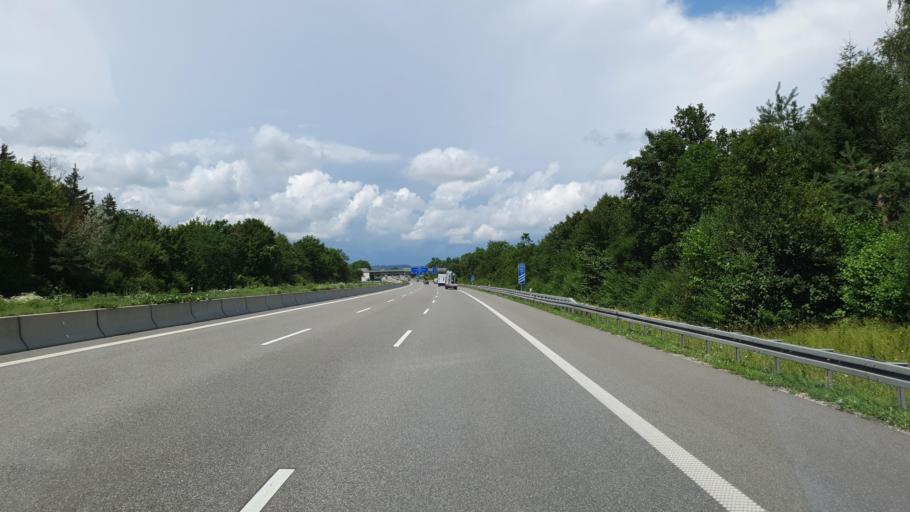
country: DE
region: Baden-Wuerttemberg
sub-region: Freiburg Region
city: Engen
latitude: 47.8511
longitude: 8.8045
